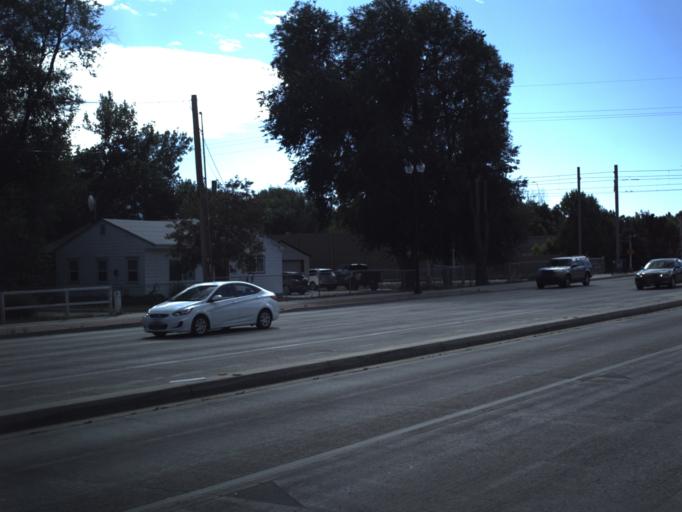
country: US
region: Utah
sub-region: Salt Lake County
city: West Jordan
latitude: 40.6050
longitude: -111.9389
